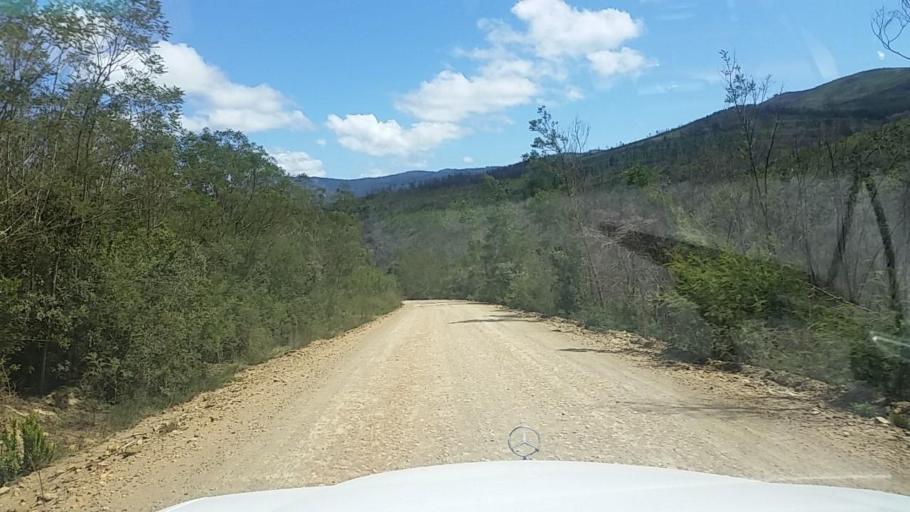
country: ZA
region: Western Cape
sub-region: Eden District Municipality
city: Knysna
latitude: -33.8588
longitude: 23.1850
